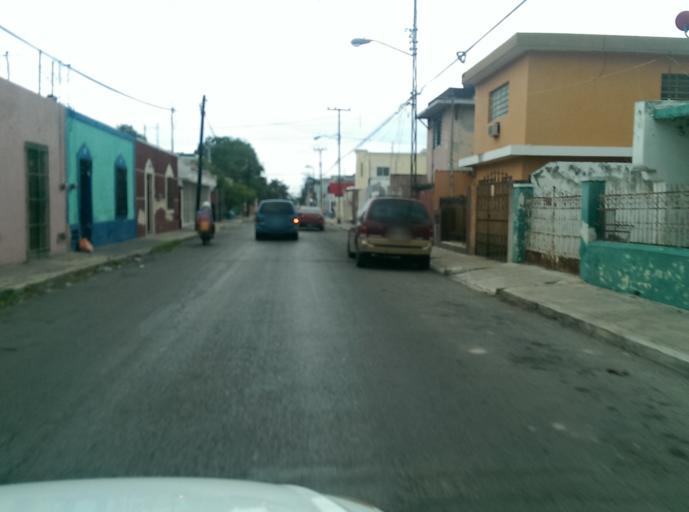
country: MX
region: Yucatan
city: Merida
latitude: 20.9779
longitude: -89.6351
